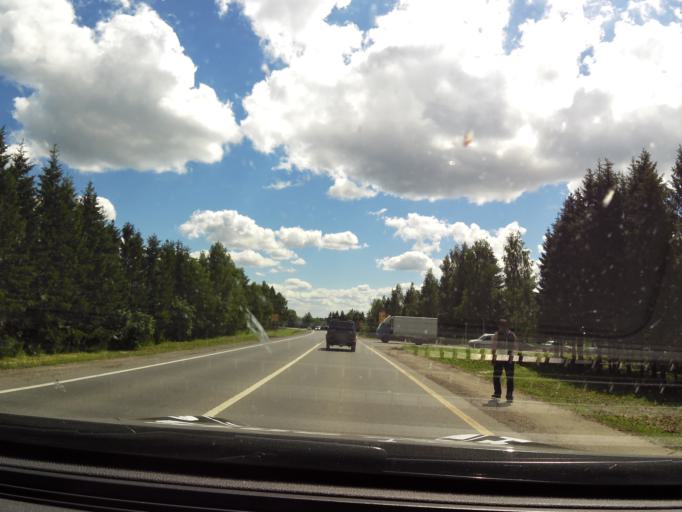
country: RU
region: Vologda
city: Molochnoye
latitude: 59.2878
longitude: 39.6923
